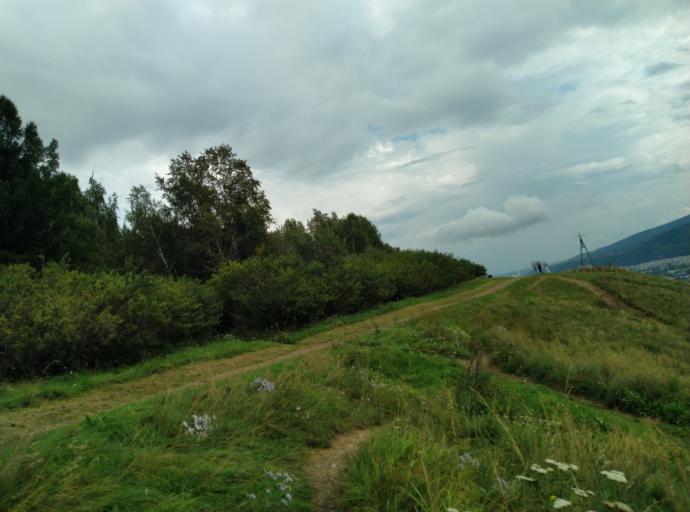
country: RU
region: Krasnoyarskiy
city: Krasnoyarsk
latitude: 55.9830
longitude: 92.7502
